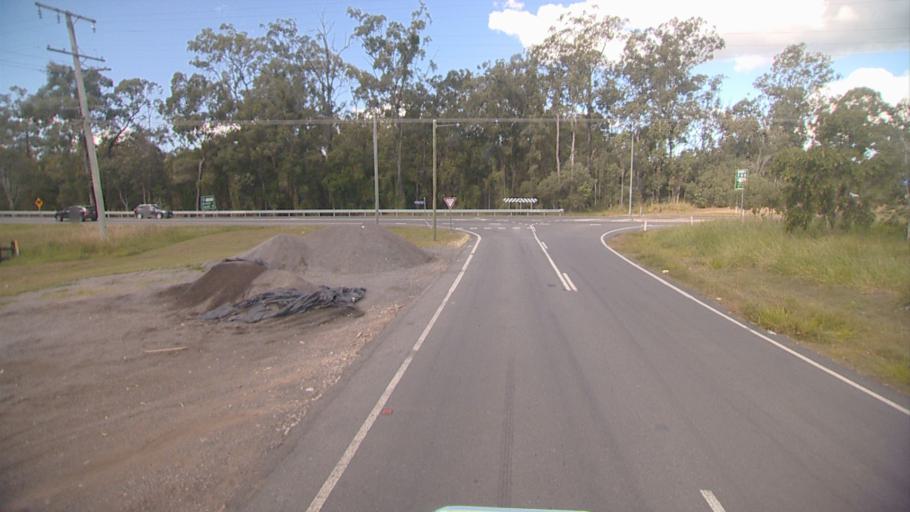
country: AU
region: Queensland
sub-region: Gold Coast
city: Yatala
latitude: -27.6752
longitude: 153.2278
